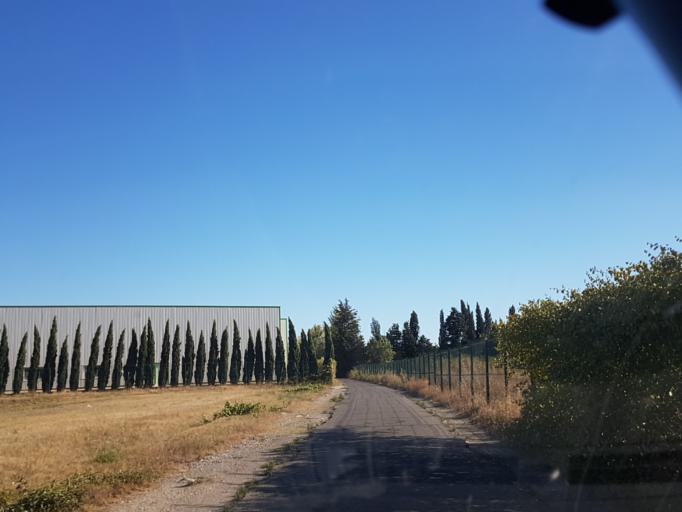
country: FR
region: Provence-Alpes-Cote d'Azur
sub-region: Departement du Vaucluse
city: Entraigues-sur-la-Sorgue
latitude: 43.9858
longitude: 4.9280
